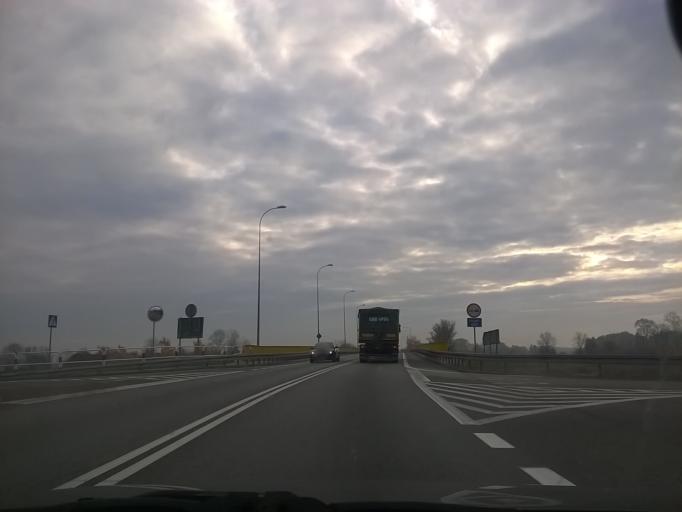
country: PL
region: Warmian-Masurian Voivodeship
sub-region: Powiat elblaski
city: Gronowo Elblaskie
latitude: 54.1717
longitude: 19.2489
